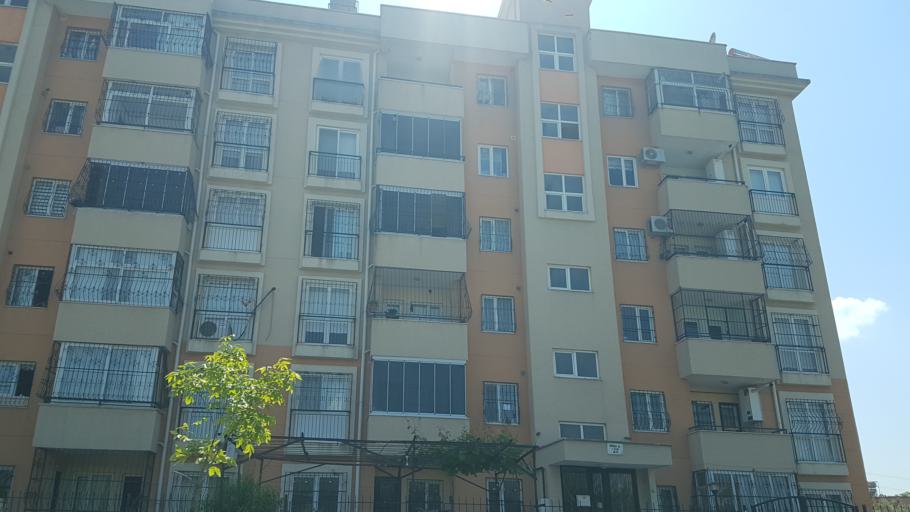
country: TR
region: Adana
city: Yuregir
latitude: 37.0187
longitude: 35.3739
